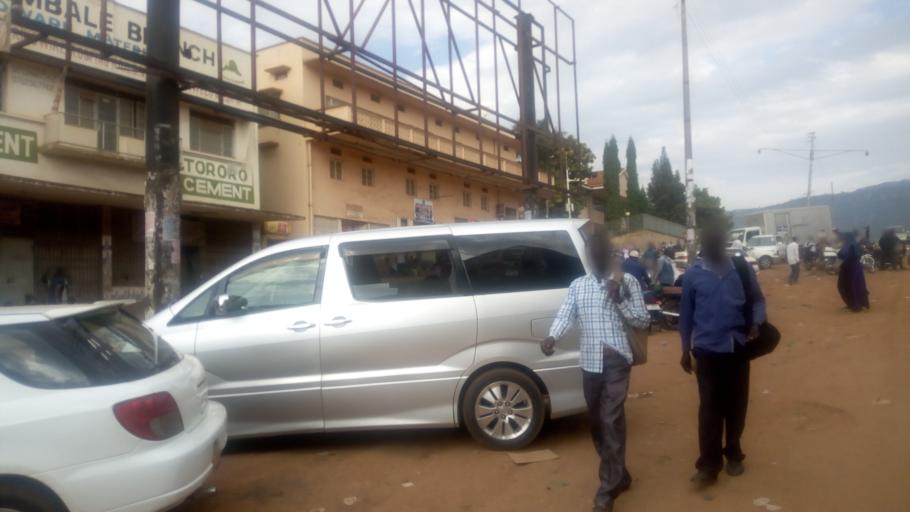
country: UG
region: Eastern Region
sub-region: Mbale District
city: Mbale
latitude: 1.0711
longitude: 34.1787
